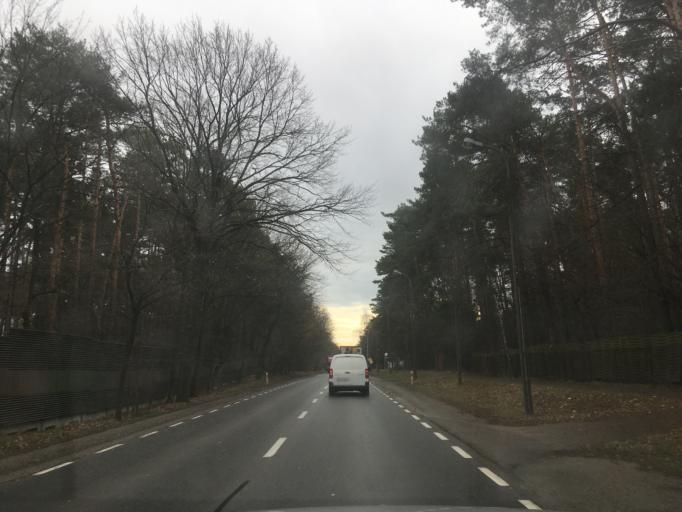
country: PL
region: Masovian Voivodeship
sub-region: Powiat piaseczynski
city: Lesznowola
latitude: 52.0992
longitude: 20.9026
